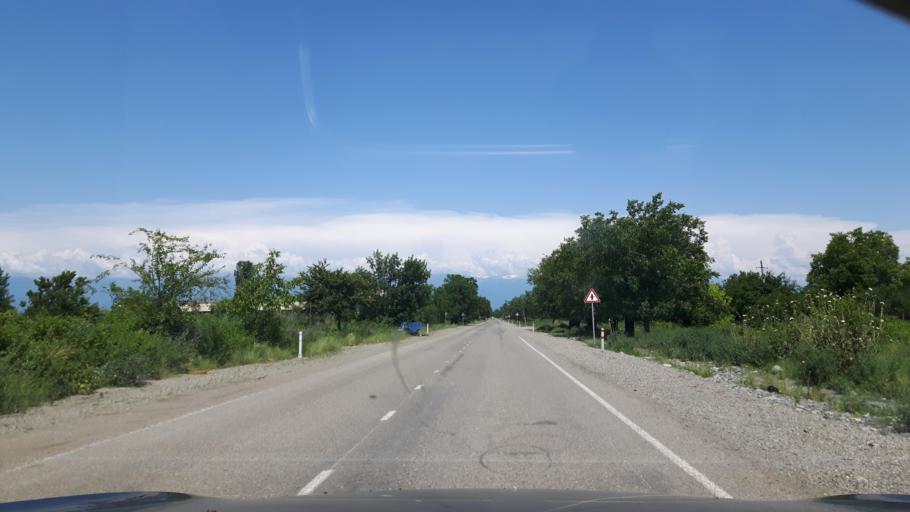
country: GE
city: Tsnori
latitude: 41.6237
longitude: 46.0096
